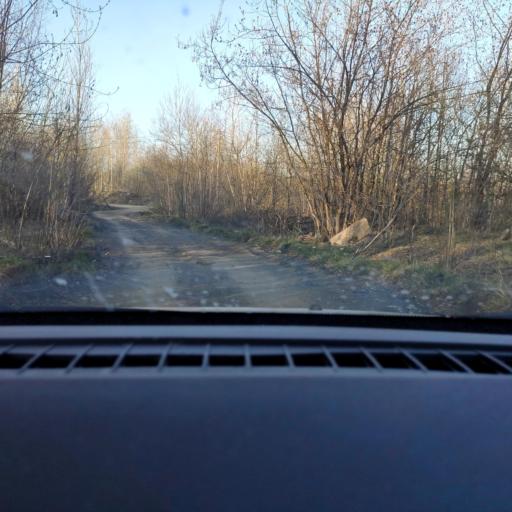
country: RU
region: Perm
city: Perm
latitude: 58.0239
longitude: 56.2099
